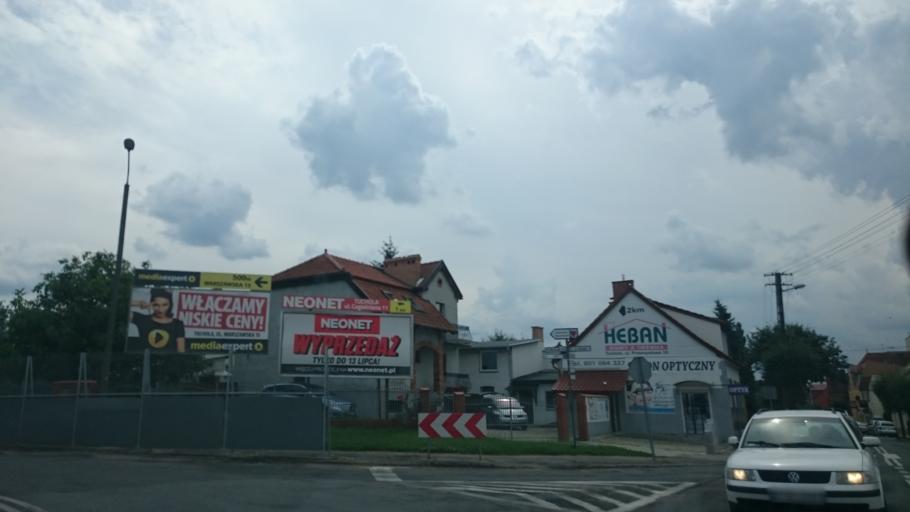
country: PL
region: Kujawsko-Pomorskie
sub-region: Powiat tucholski
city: Tuchola
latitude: 53.5908
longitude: 17.8649
